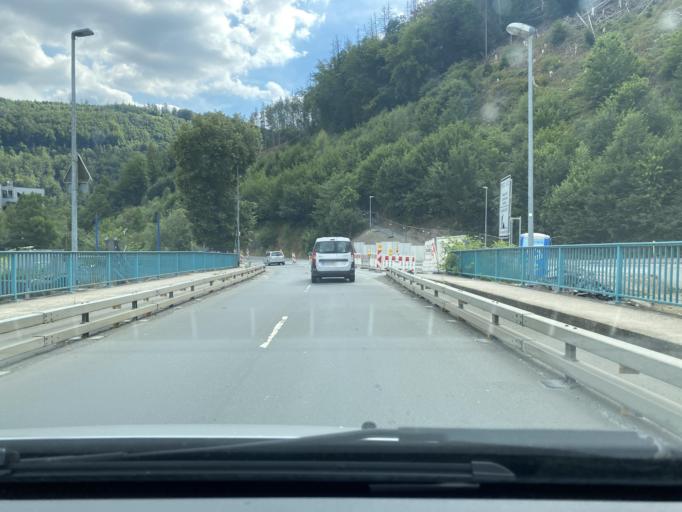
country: DE
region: North Rhine-Westphalia
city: Werdohl
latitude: 51.2550
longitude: 7.7539
